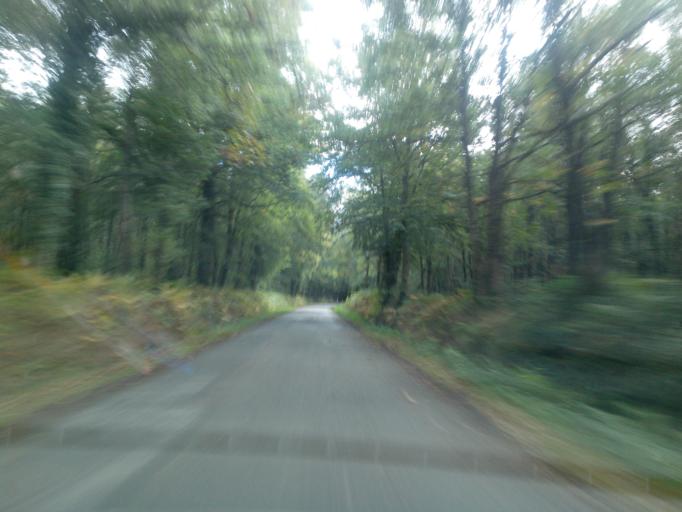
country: FR
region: Brittany
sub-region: Departement du Morbihan
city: Guilliers
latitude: 48.0979
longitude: -2.3754
